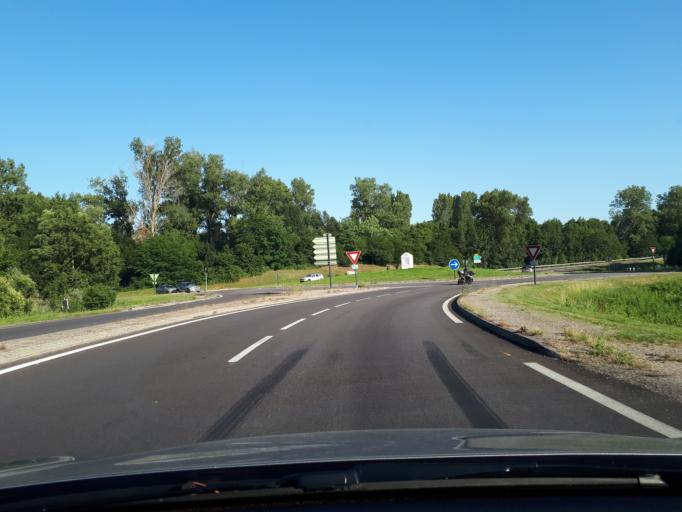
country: FR
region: Rhone-Alpes
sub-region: Departement de l'Isere
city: La Verpilliere
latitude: 45.6381
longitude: 5.1572
